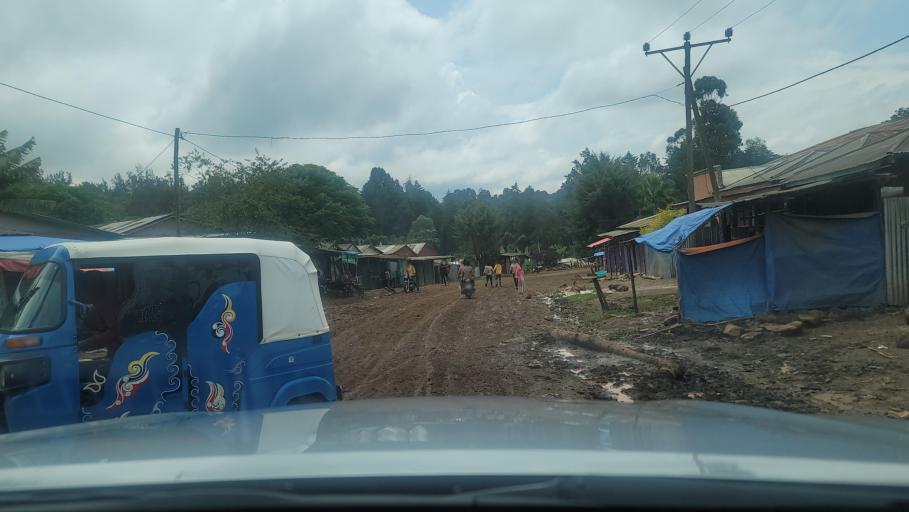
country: ET
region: Oromiya
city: Agaro
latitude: 7.7879
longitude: 36.4219
